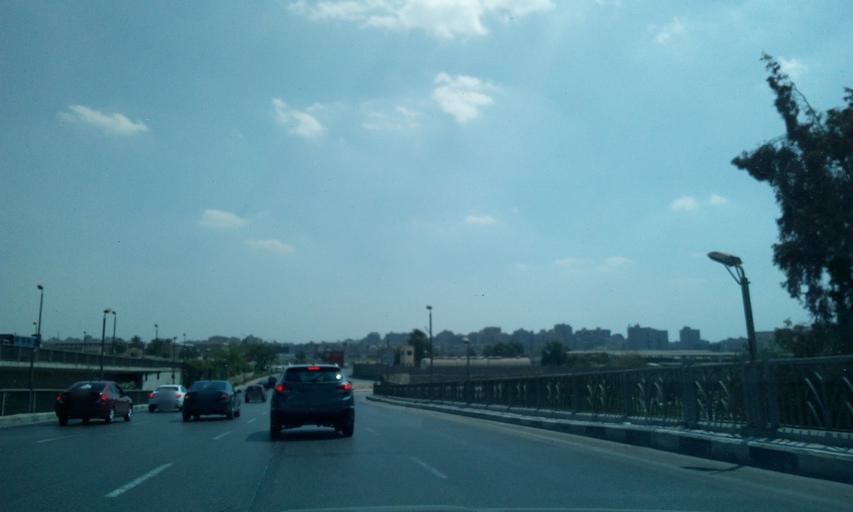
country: EG
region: Muhafazat al Qahirah
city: Cairo
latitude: 30.0792
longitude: 31.3616
